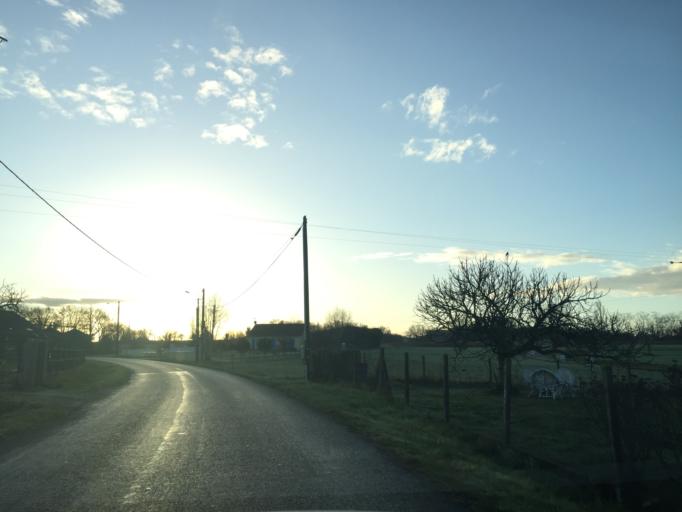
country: FR
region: Aquitaine
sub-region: Departement de la Dordogne
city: Saint-Aulaye
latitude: 45.2540
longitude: 0.2011
